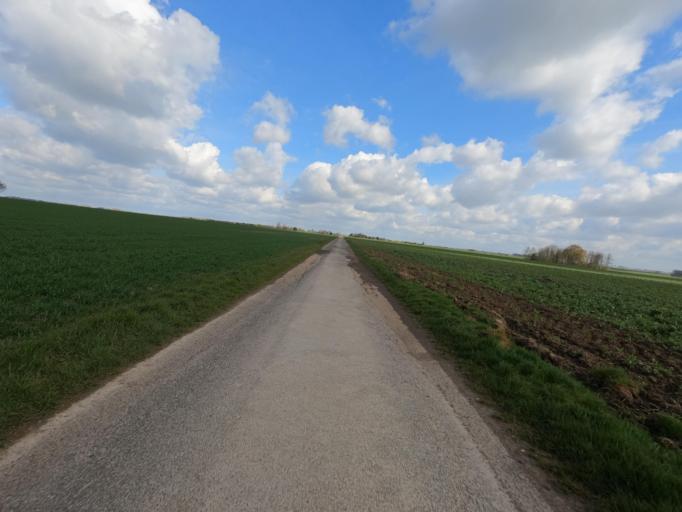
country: DE
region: North Rhine-Westphalia
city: Erkelenz
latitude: 51.0157
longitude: 6.3451
